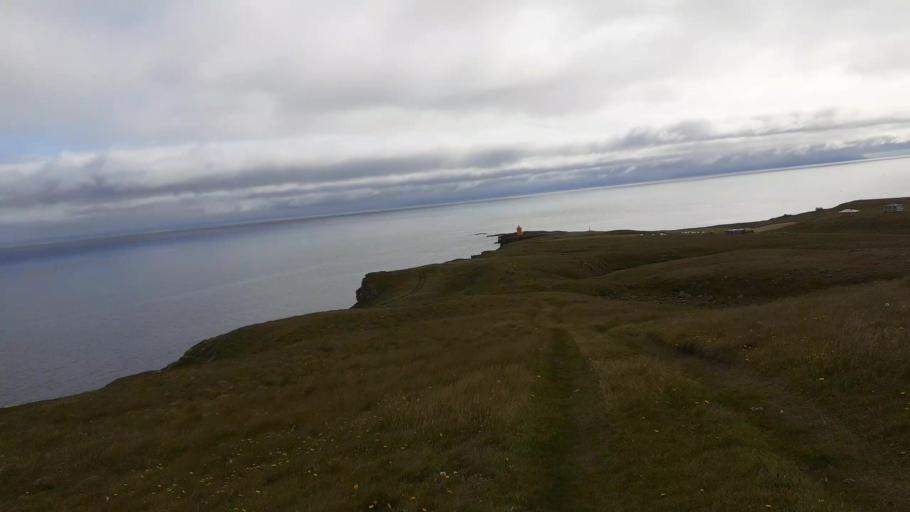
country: IS
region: Northeast
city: Dalvik
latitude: 66.5344
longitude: -17.9831
